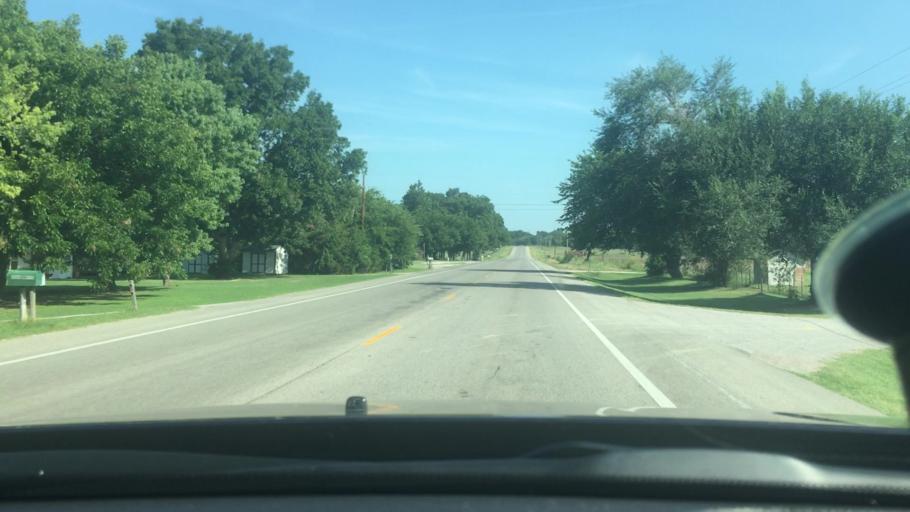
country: US
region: Oklahoma
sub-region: Garvin County
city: Wynnewood
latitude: 34.6727
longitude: -97.2068
